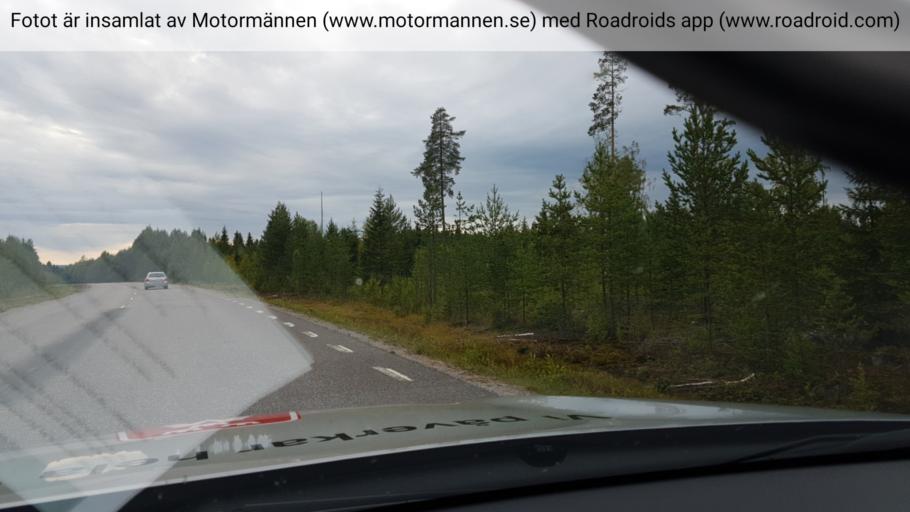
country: SE
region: Norrbotten
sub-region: Lulea Kommun
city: Gammelstad
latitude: 65.6625
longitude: 22.0679
